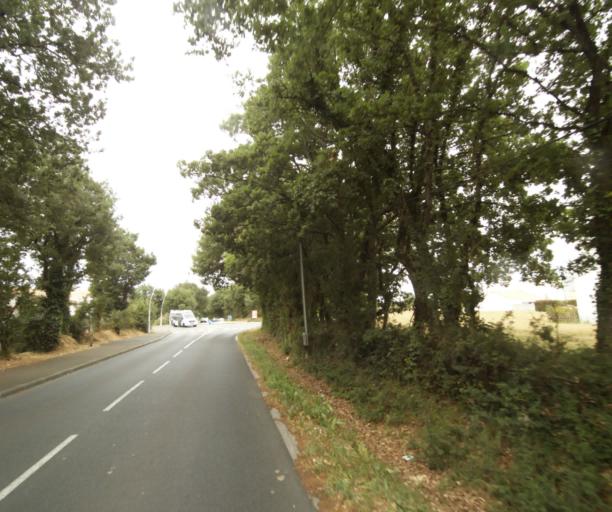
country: FR
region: Pays de la Loire
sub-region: Departement de la Vendee
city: Chateau-d'Olonne
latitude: 46.5088
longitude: -1.7396
